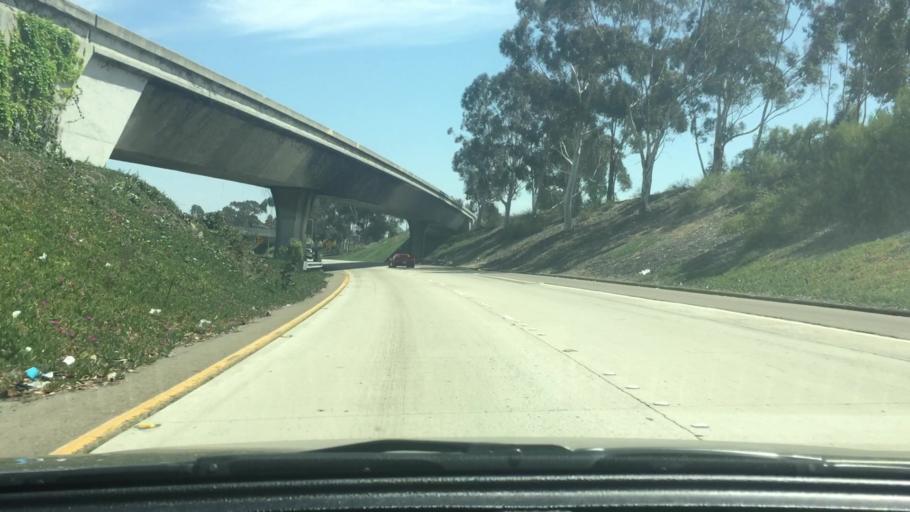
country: US
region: California
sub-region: San Diego County
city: National City
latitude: 32.7146
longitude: -117.1032
